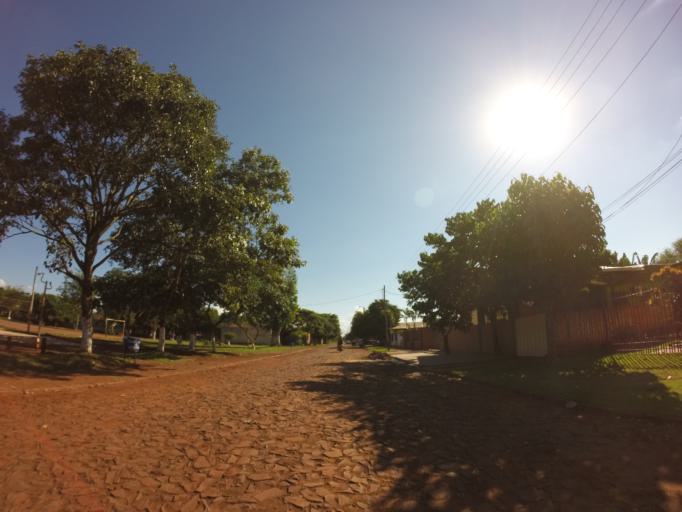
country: PY
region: Alto Parana
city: Ciudad del Este
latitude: -25.3749
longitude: -54.6486
